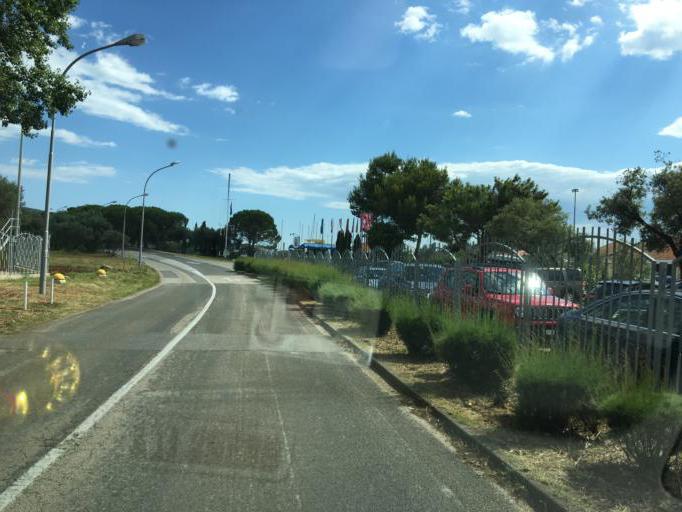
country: HR
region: Primorsko-Goranska
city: Punat
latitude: 45.0302
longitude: 14.6290
